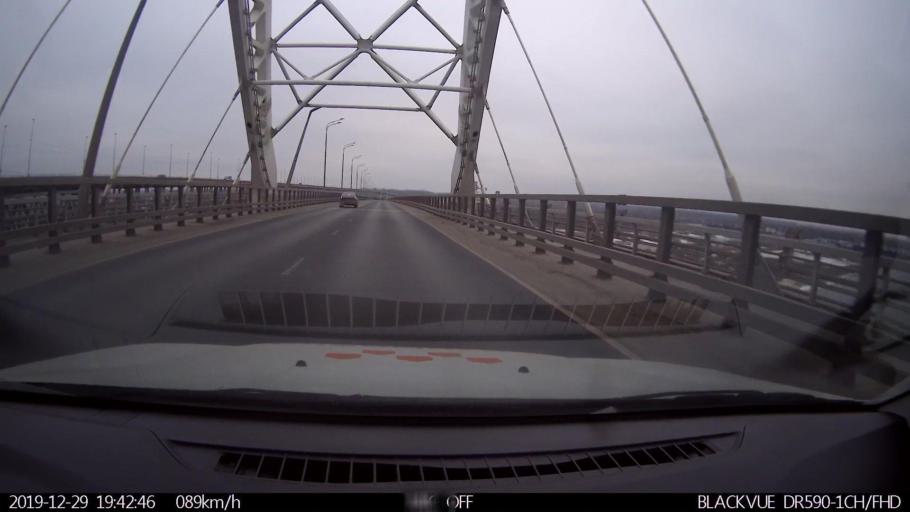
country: RU
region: Nizjnij Novgorod
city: Neklyudovo
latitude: 56.3538
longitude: 43.9258
